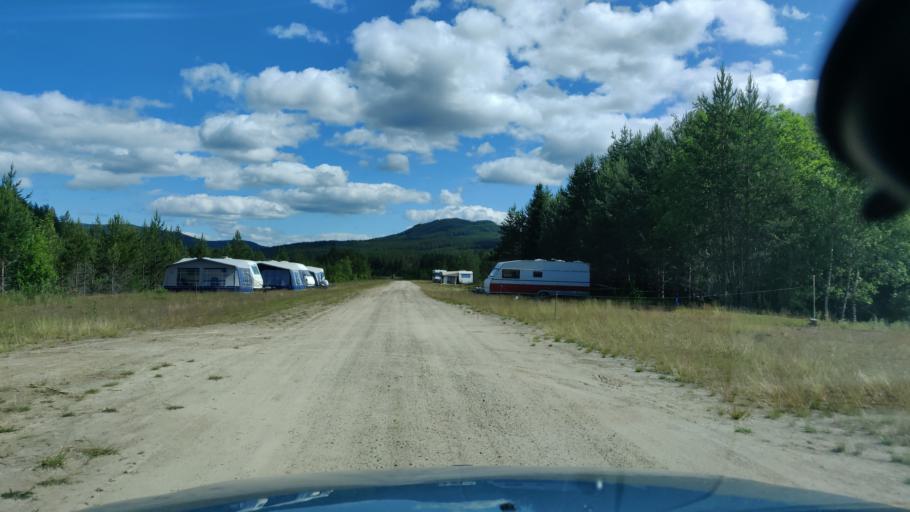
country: NO
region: Hedmark
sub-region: Trysil
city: Innbygda
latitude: 60.9088
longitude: 12.5672
